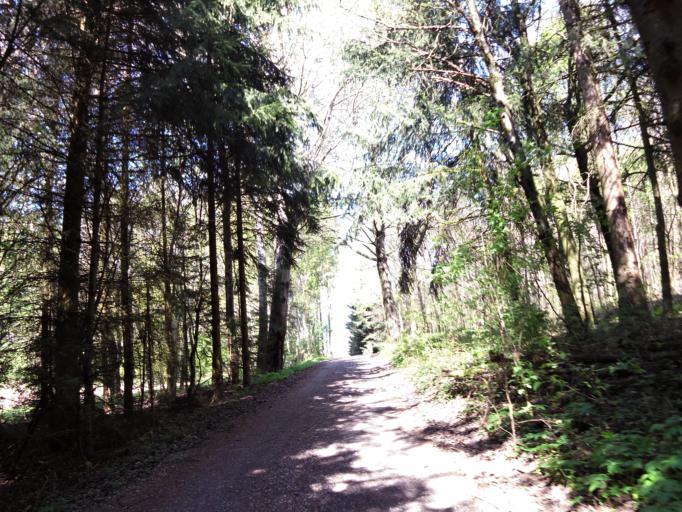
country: DE
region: Bavaria
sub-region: Upper Bavaria
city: Fraunberg
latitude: 48.3407
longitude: 12.0078
